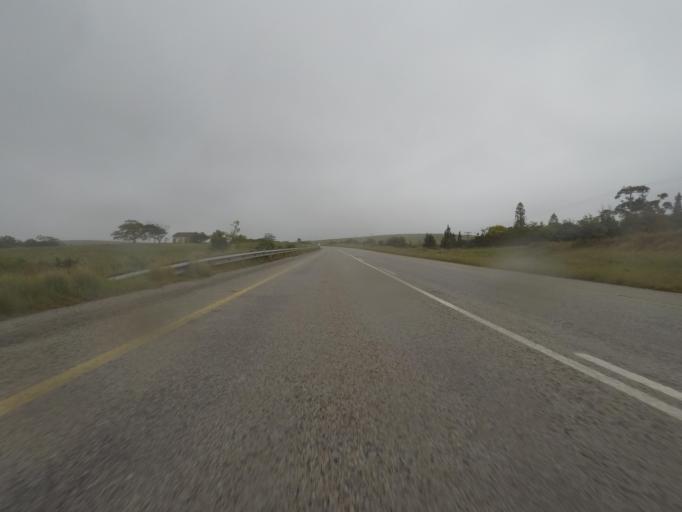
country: ZA
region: Eastern Cape
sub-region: Cacadu District Municipality
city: Grahamstown
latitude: -33.6352
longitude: 26.3187
